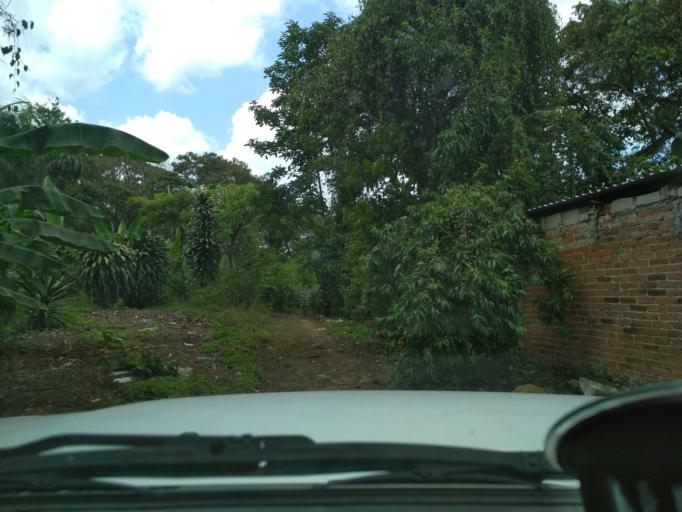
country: MX
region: Veracruz
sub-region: Fortin
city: Monte Salas
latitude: 18.9365
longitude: -97.0156
